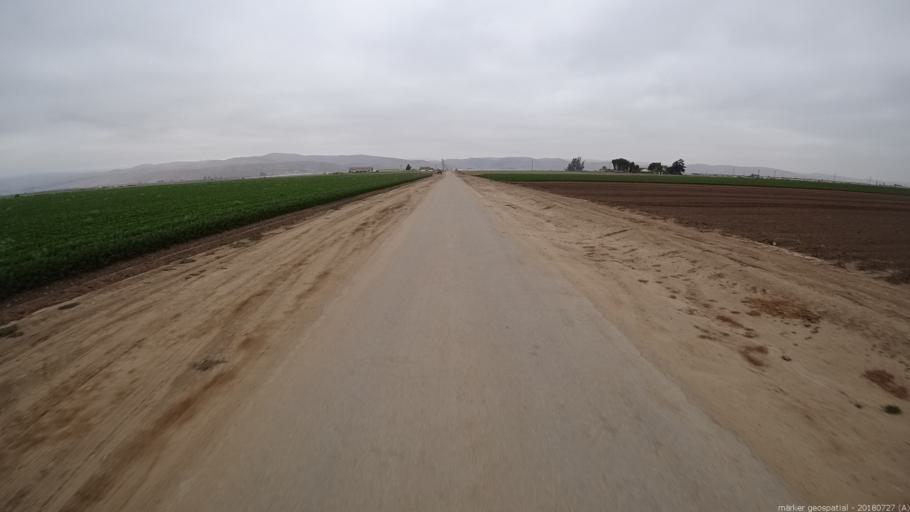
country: US
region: California
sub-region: Monterey County
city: Greenfield
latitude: 36.3362
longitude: -121.2473
